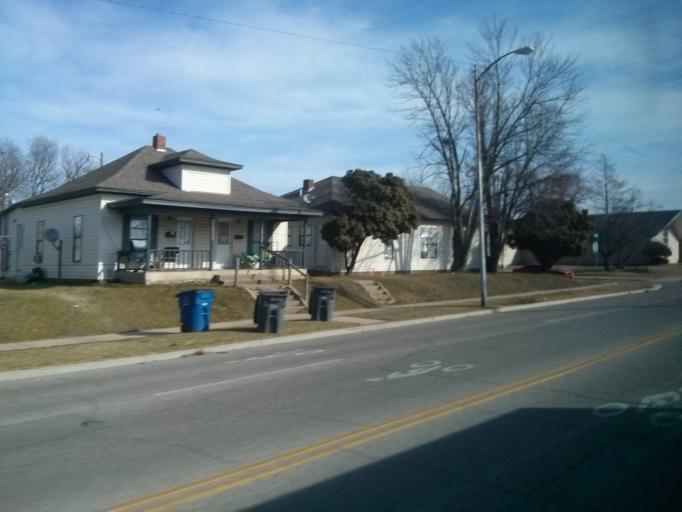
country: US
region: Oklahoma
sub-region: Tulsa County
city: Tulsa
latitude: 36.1566
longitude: -95.9626
